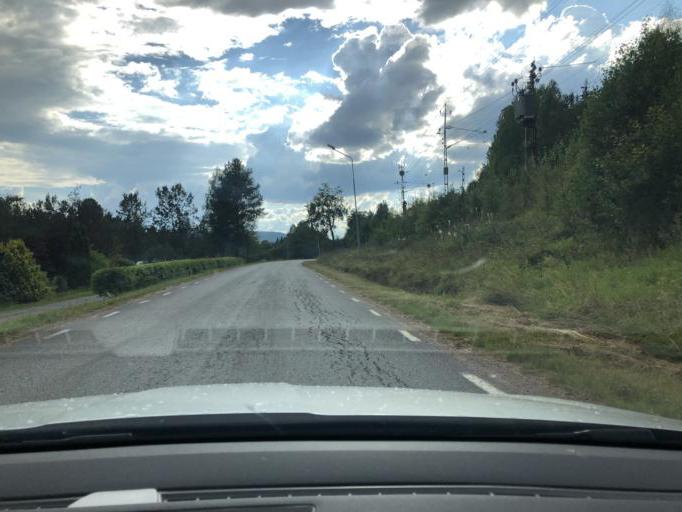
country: SE
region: Vaesternorrland
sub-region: Solleftea Kommun
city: Solleftea
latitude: 63.2131
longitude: 17.1937
